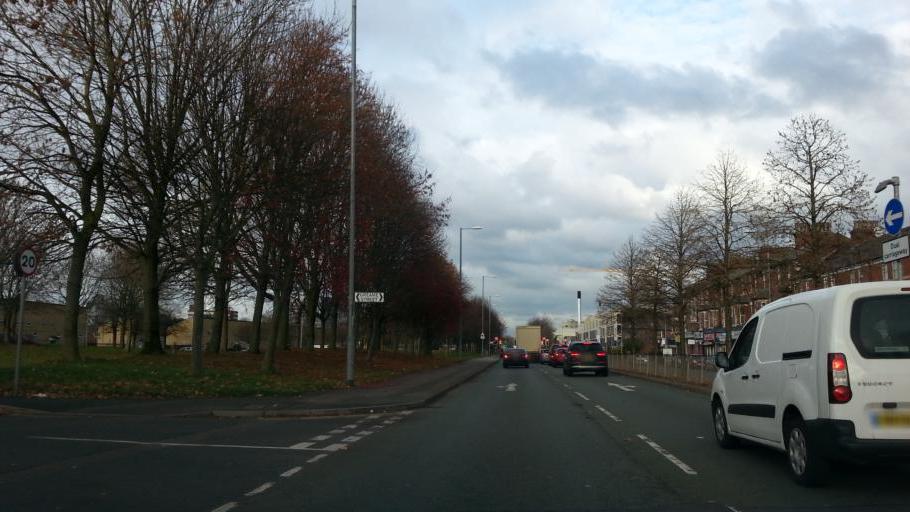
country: GB
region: England
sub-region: Manchester
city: Hulme
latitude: 53.4551
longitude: -2.2453
